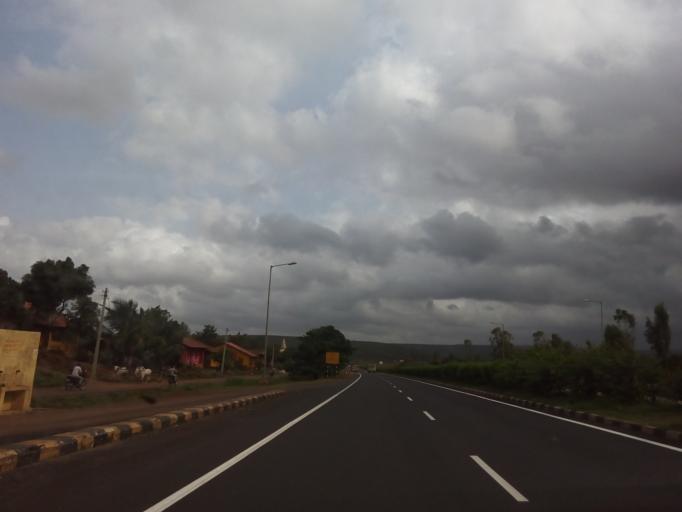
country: IN
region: Karnataka
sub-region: Belgaum
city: Hukeri
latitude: 16.0807
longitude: 74.5181
